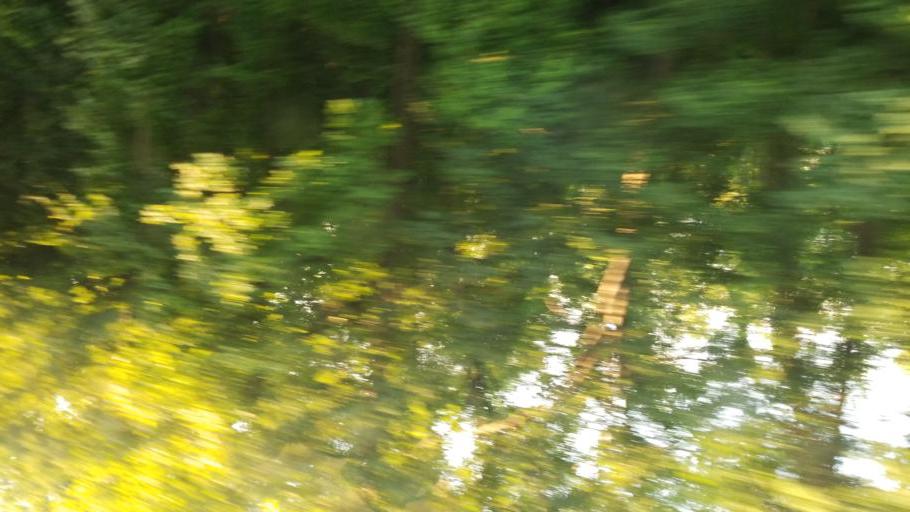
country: US
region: Virginia
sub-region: Fairfax County
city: Springfield
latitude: 38.7929
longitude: -77.1678
